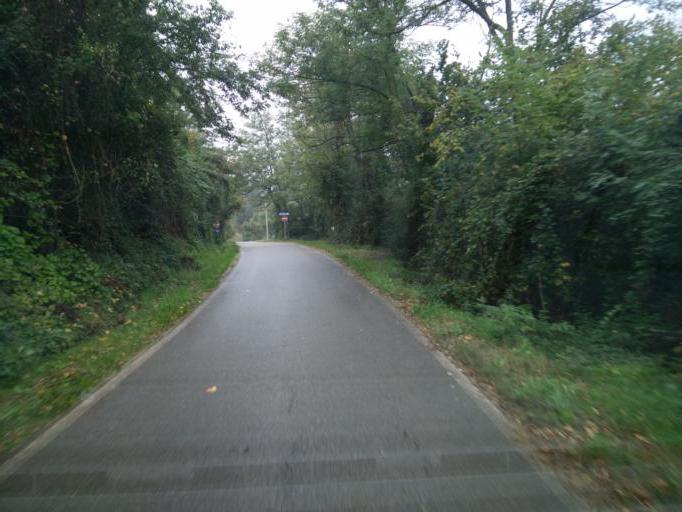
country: IT
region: Emilia-Romagna
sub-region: Provincia di Bologna
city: Marzabotto
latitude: 44.3130
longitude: 11.1852
